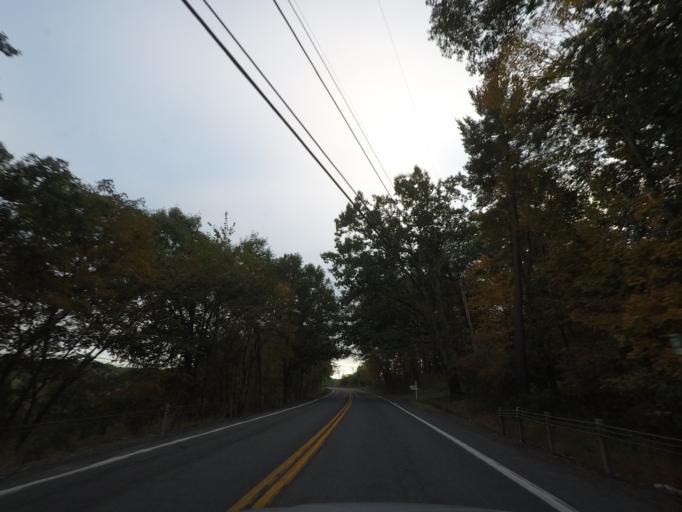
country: US
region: New York
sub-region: Rensselaer County
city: Nassau
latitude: 42.5697
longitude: -73.6262
